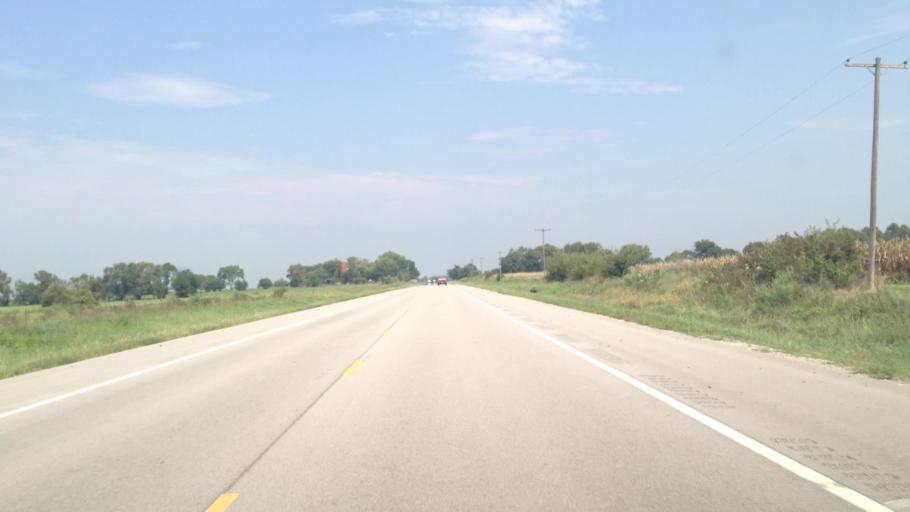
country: US
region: Kansas
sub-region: Labette County
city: Altamont
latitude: 37.2380
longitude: -95.2672
